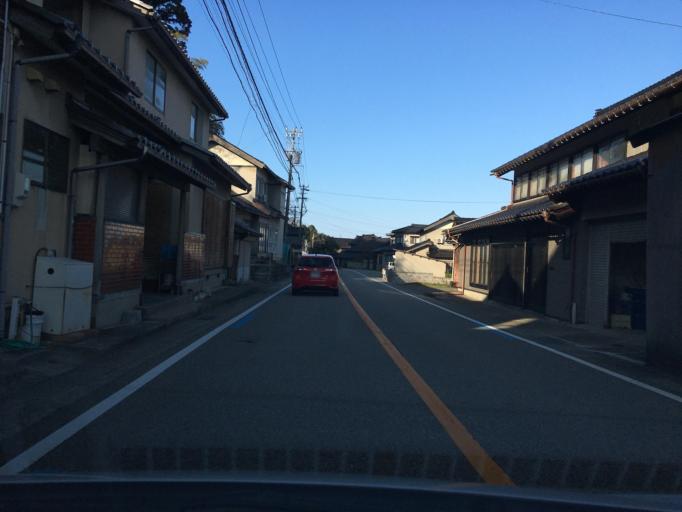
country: JP
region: Toyama
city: Himi
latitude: 36.9495
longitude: 137.0379
